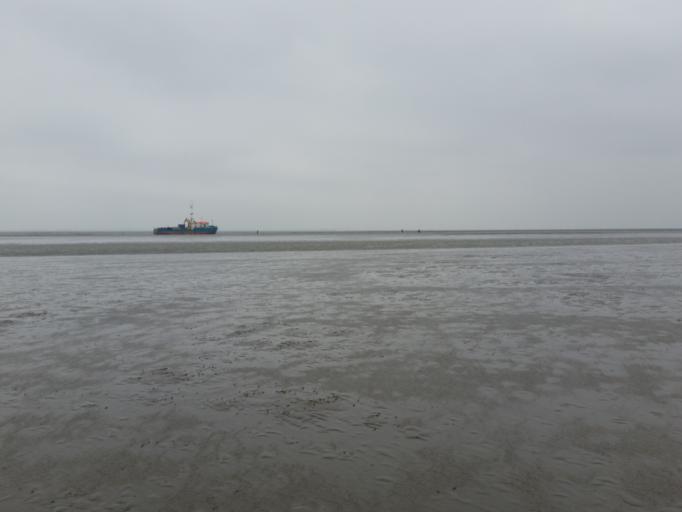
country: NL
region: Friesland
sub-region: Gemeente Dongeradeel
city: Holwerd
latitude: 53.4350
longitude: 5.9007
